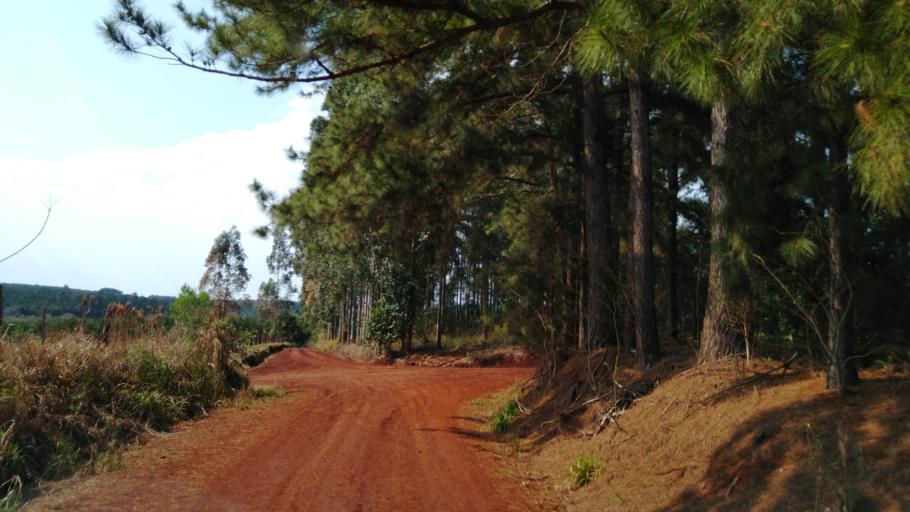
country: AR
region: Misiones
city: Capiovi
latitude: -26.9528
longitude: -55.0449
